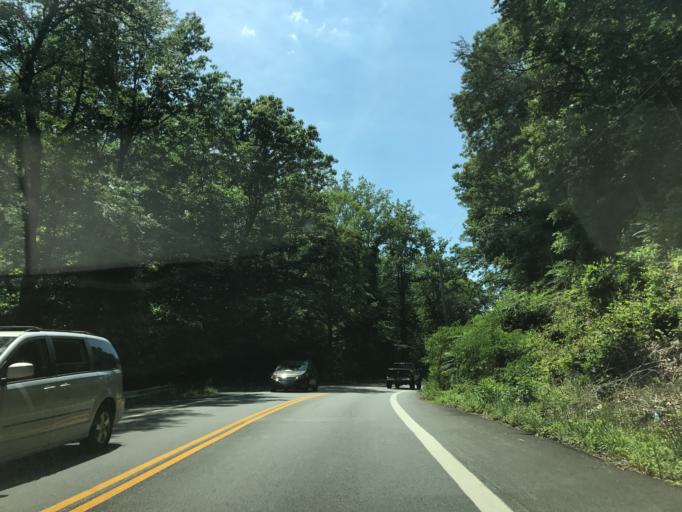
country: US
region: Maryland
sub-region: Anne Arundel County
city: Crownsville
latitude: 38.9860
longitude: -76.6192
